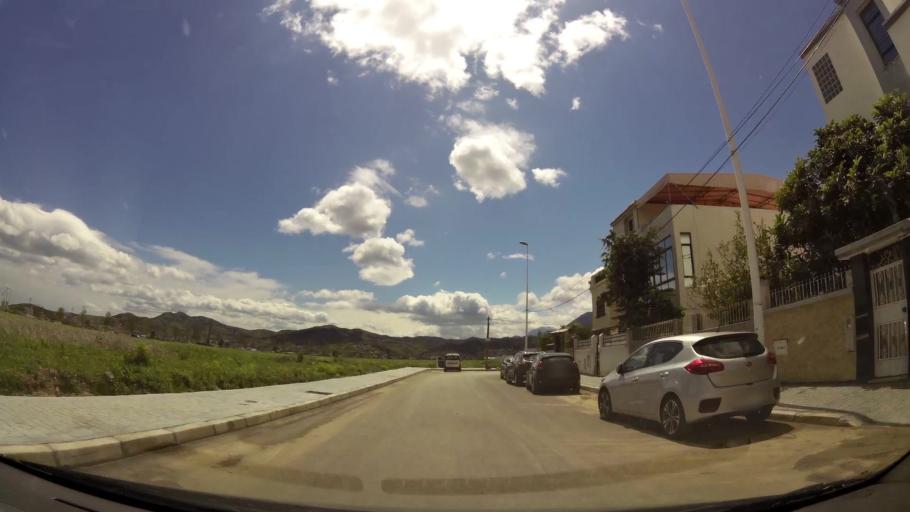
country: MA
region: Tanger-Tetouan
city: Tetouan
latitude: 35.5804
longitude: -5.3330
